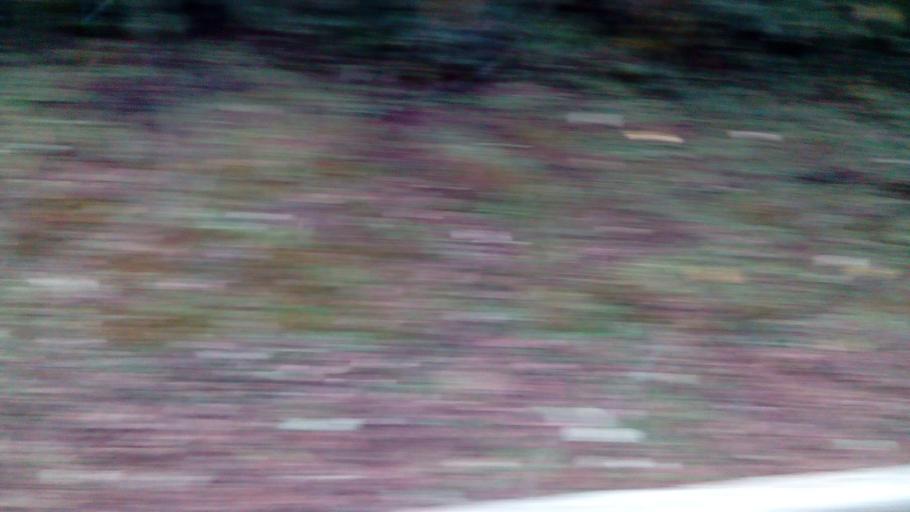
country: TW
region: Taiwan
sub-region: Hualien
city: Hualian
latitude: 24.3962
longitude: 121.3594
